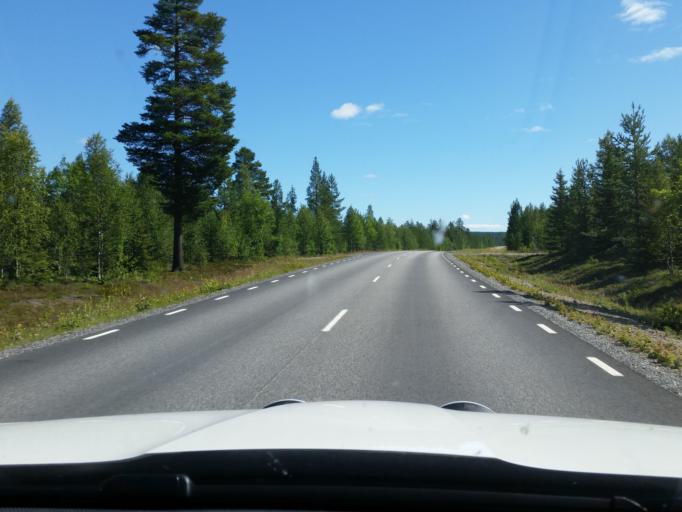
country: SE
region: Vaesterbotten
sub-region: Skelleftea Kommun
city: Storvik
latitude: 65.3284
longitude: 20.6634
